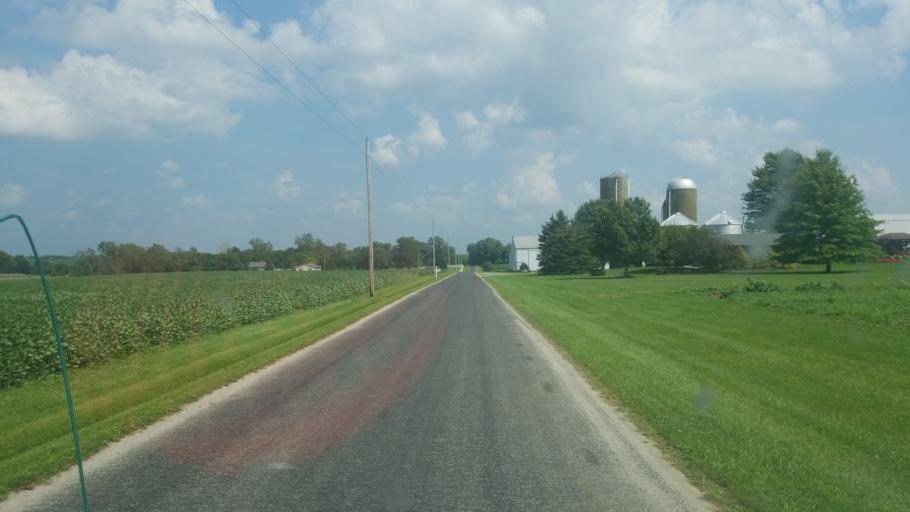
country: US
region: Ohio
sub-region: Huron County
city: New London
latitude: 41.0470
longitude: -82.4483
